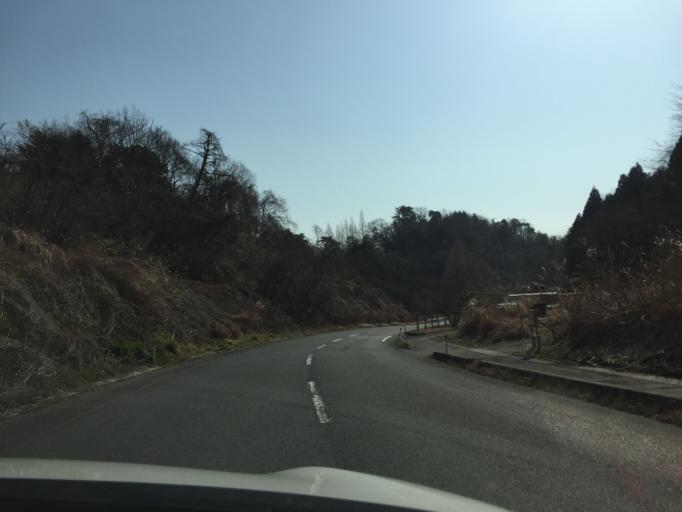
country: JP
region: Fukushima
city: Iwaki
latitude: 36.9715
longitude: 140.9285
